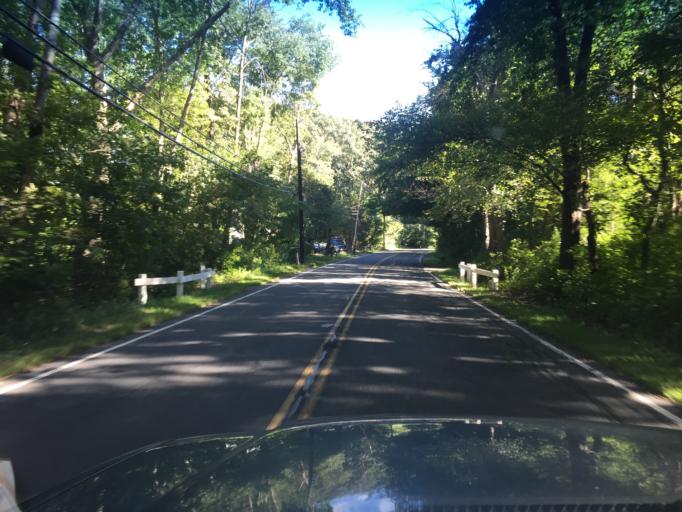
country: US
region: Massachusetts
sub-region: Norfolk County
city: Medway
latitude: 42.1686
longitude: -71.4108
